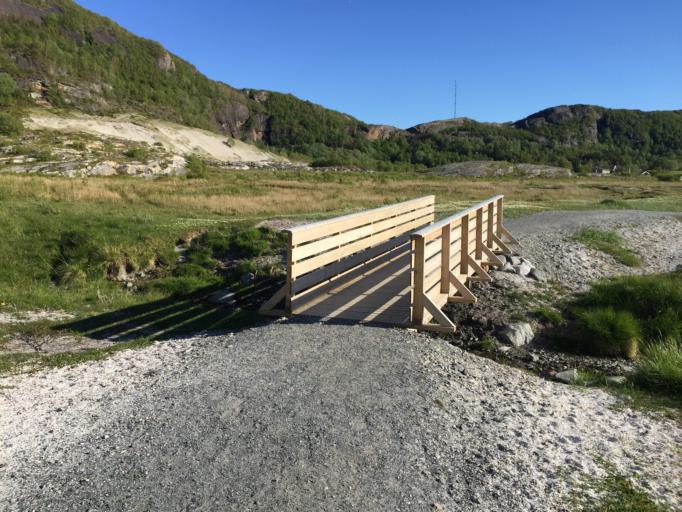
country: NO
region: Nordland
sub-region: Bodo
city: Loding
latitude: 67.4136
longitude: 14.6336
